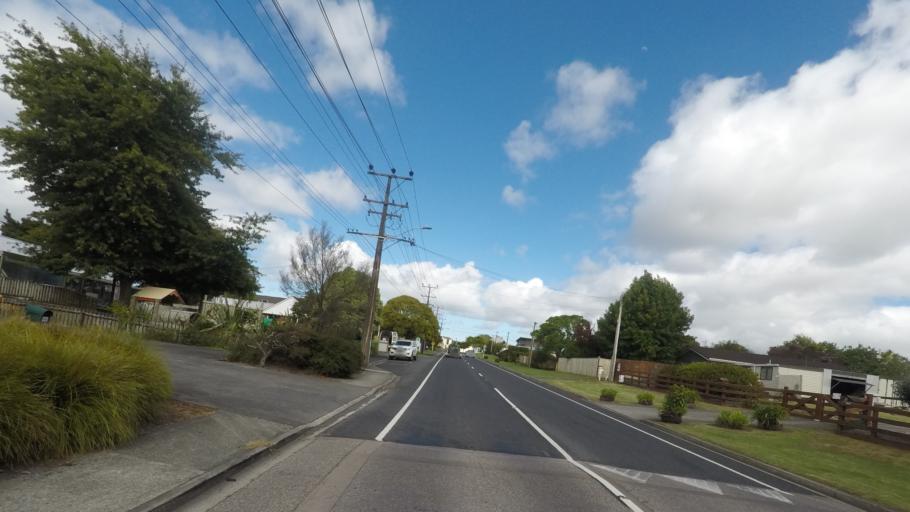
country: NZ
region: Auckland
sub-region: Auckland
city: Muriwai Beach
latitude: -36.7708
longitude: 174.5479
